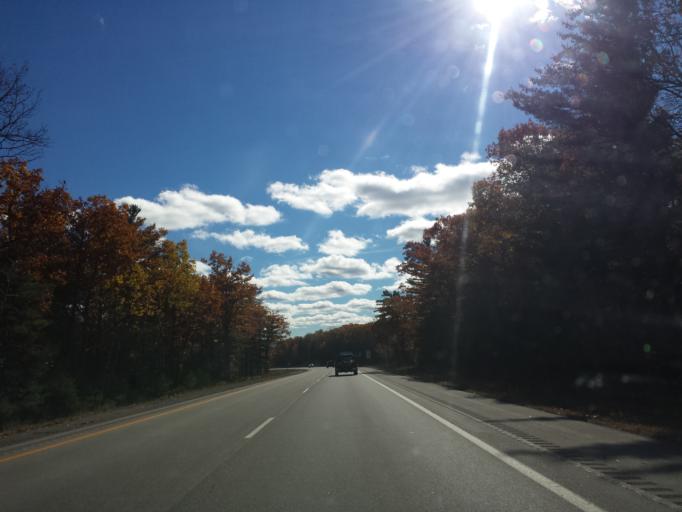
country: US
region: Michigan
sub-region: Cheboygan County
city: Indian River
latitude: 45.4375
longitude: -84.6074
